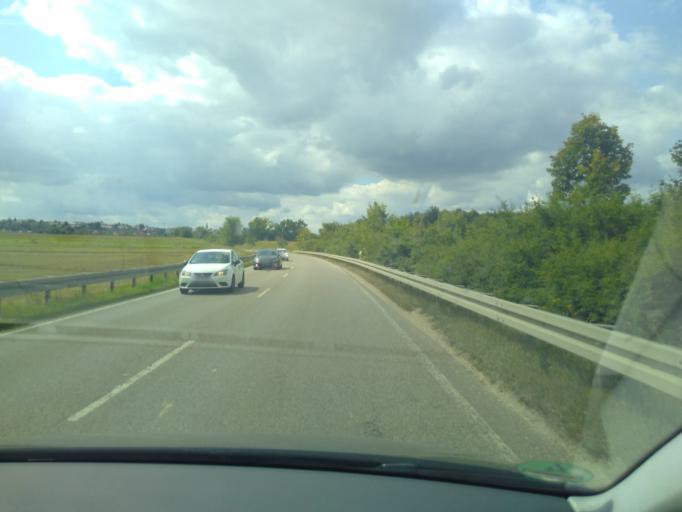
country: DE
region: Baden-Wuerttemberg
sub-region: Tuebingen Region
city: Merklingen
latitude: 48.5089
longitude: 9.7413
